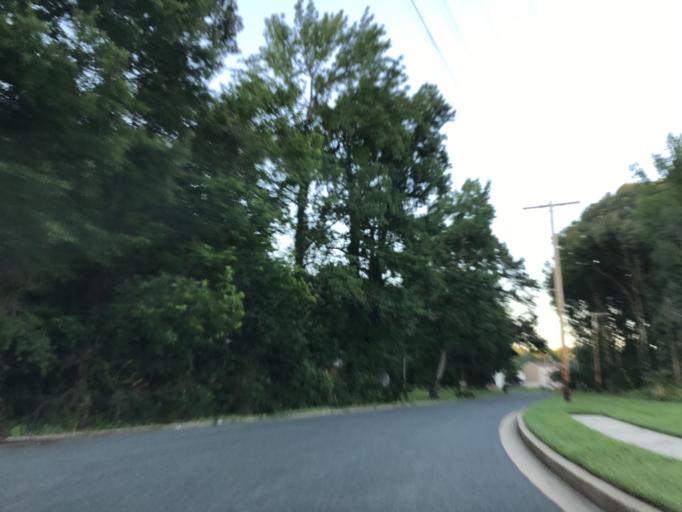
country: US
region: Maryland
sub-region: Baltimore County
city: Bowleys Quarters
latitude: 39.3346
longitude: -76.3897
